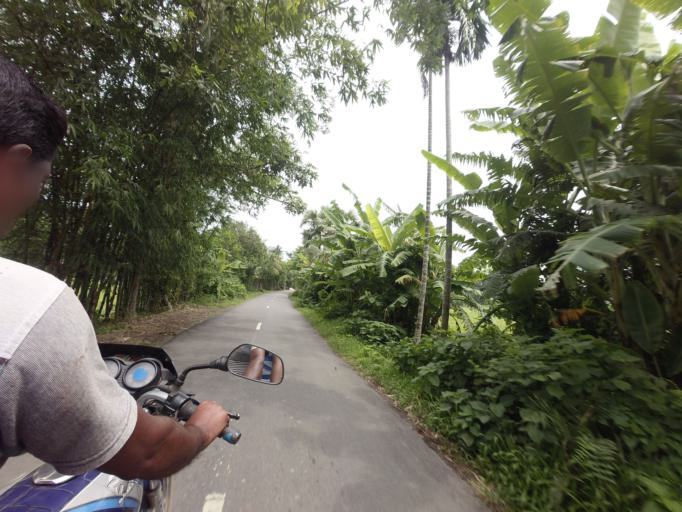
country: BD
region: Khulna
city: Kalia
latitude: 23.0902
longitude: 89.6577
